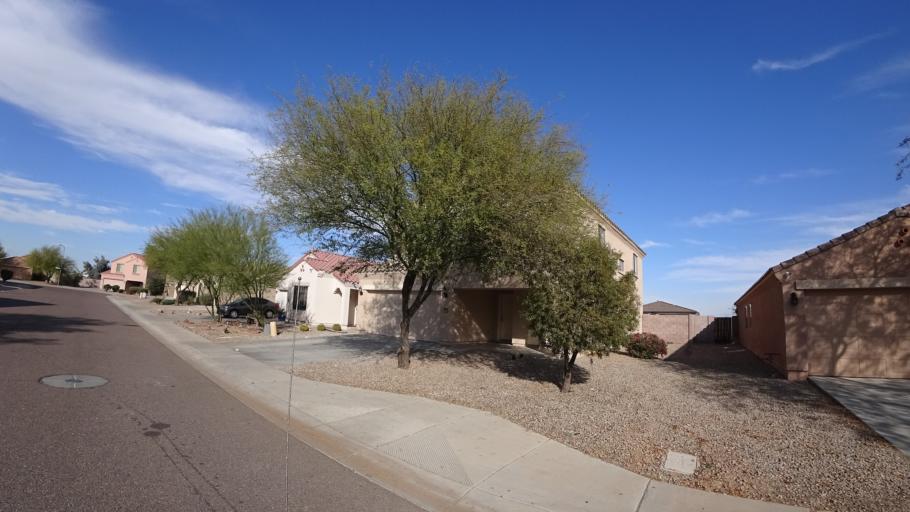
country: US
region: Arizona
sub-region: Maricopa County
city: Tolleson
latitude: 33.4321
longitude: -112.2859
